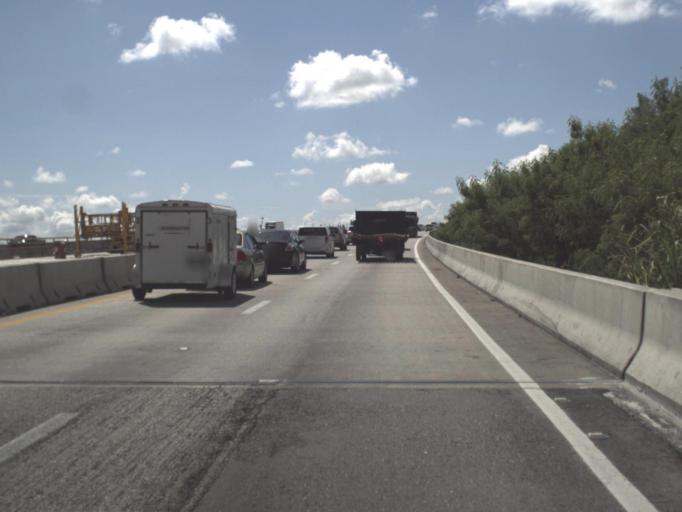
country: US
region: Florida
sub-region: Lee County
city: Tice
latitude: 26.7019
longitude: -81.8017
